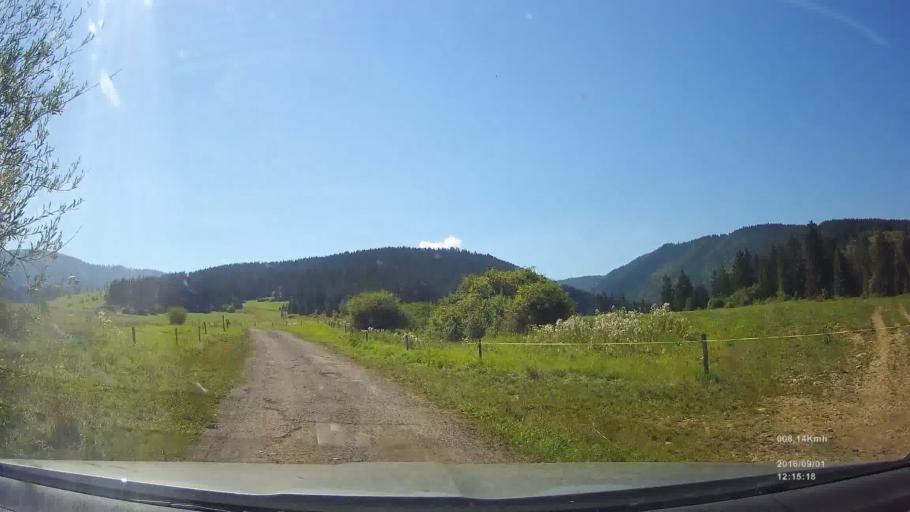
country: SK
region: Zilinsky
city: Ruzomberok
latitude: 49.0467
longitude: 19.4291
